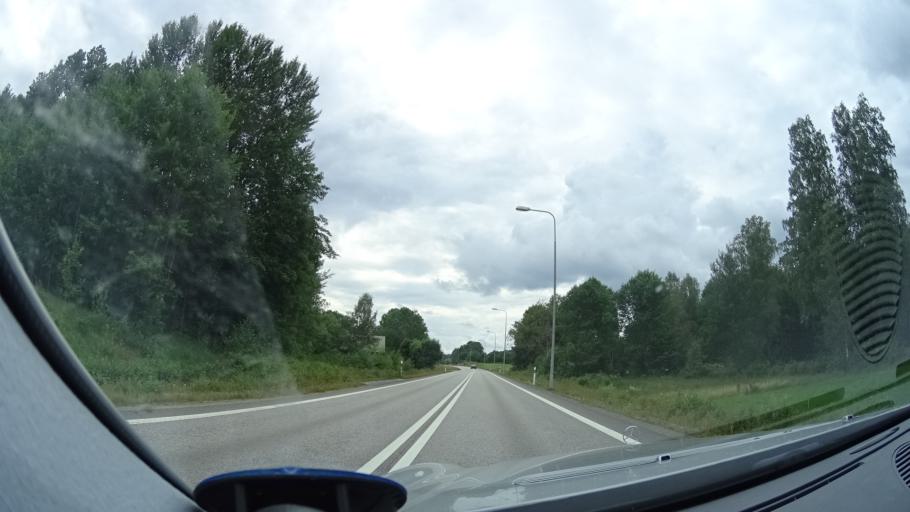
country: SE
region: Kronoberg
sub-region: Tingsryds Kommun
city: Tingsryd
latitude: 56.4989
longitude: 15.0610
